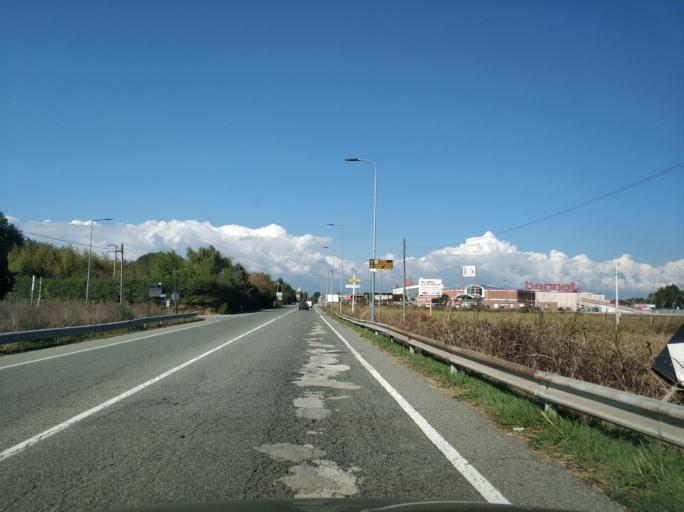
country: IT
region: Piedmont
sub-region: Provincia di Torino
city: Borgaro Torinese
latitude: 45.1648
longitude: 7.6546
